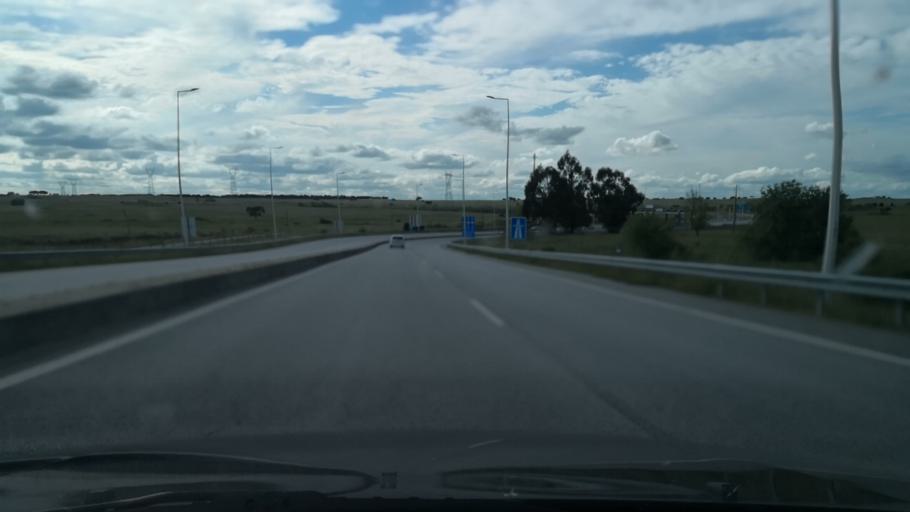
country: PT
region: Evora
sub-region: Evora
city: Evora
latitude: 38.6416
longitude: -7.8526
